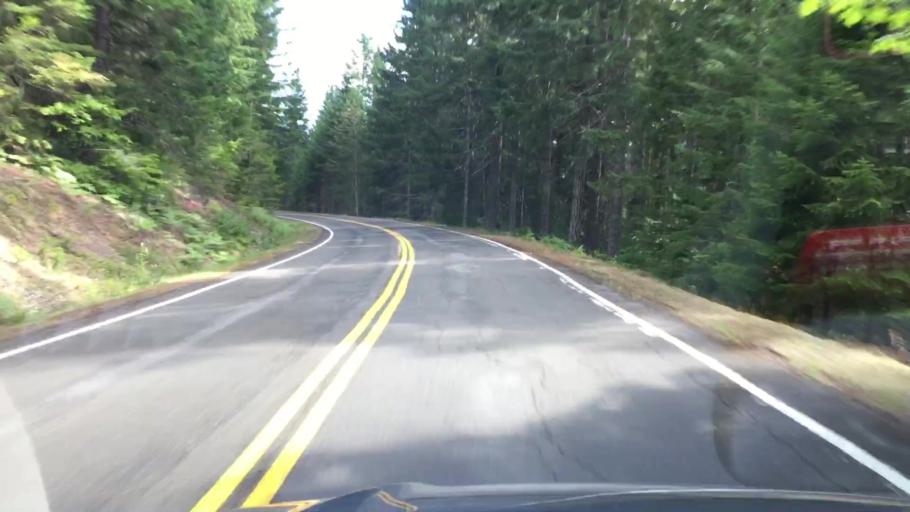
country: US
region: Washington
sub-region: Pierce County
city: Buckley
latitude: 46.7450
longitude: -121.6196
